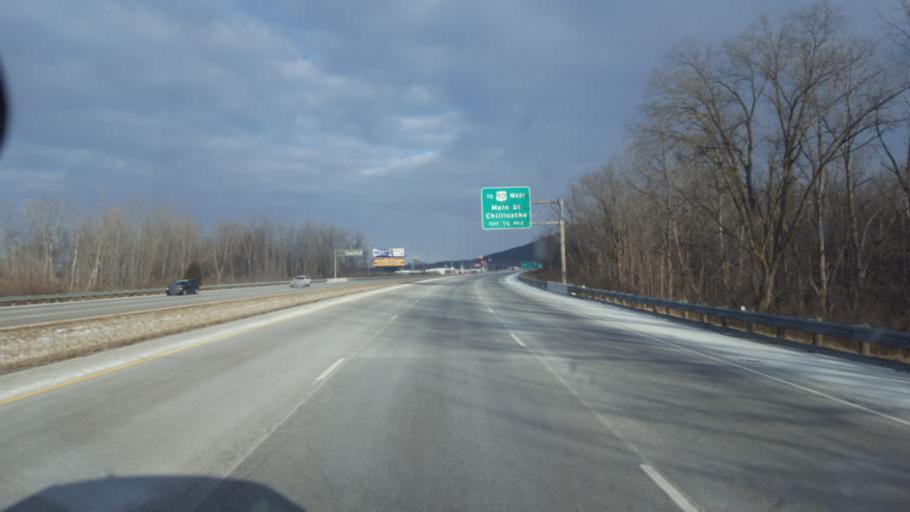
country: US
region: Ohio
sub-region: Ross County
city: Chillicothe
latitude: 39.3286
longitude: -82.9457
